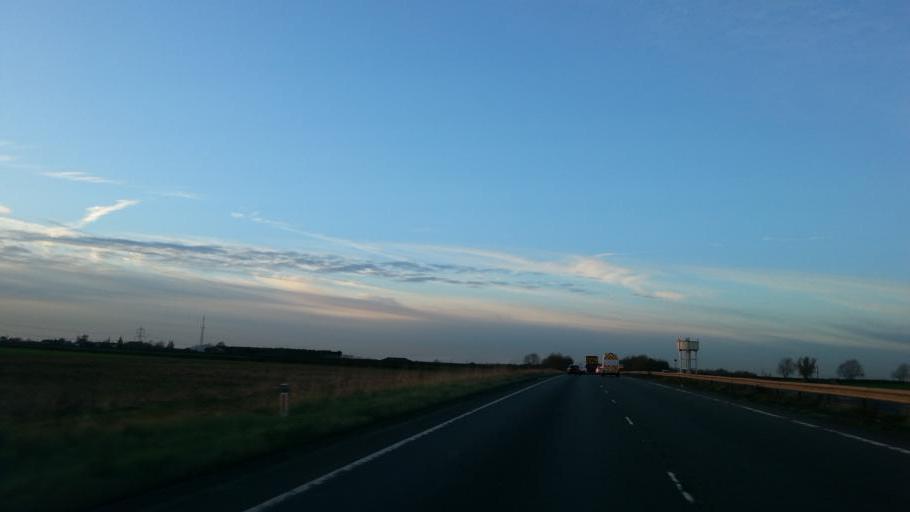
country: GB
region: England
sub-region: Lincolnshire
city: Grantham
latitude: 52.8886
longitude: -0.6449
